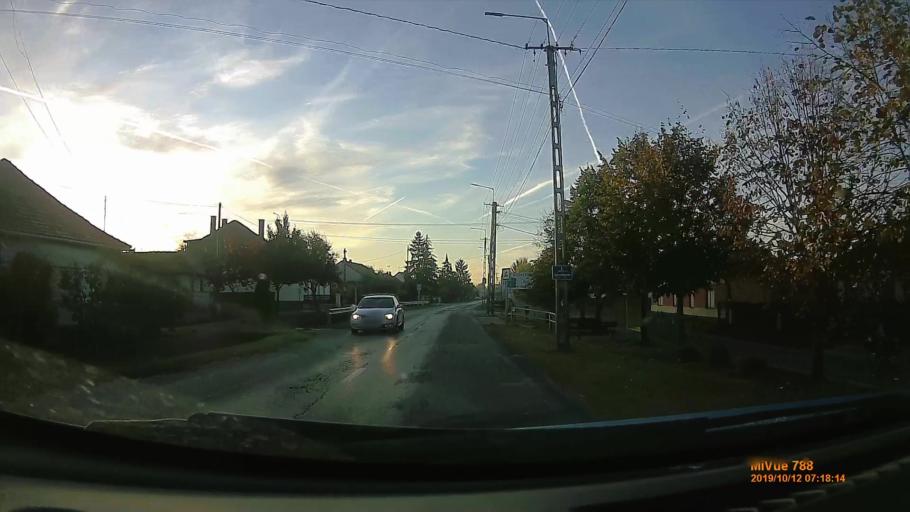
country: HU
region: Hajdu-Bihar
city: Hosszupalyi
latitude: 47.3987
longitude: 21.7266
